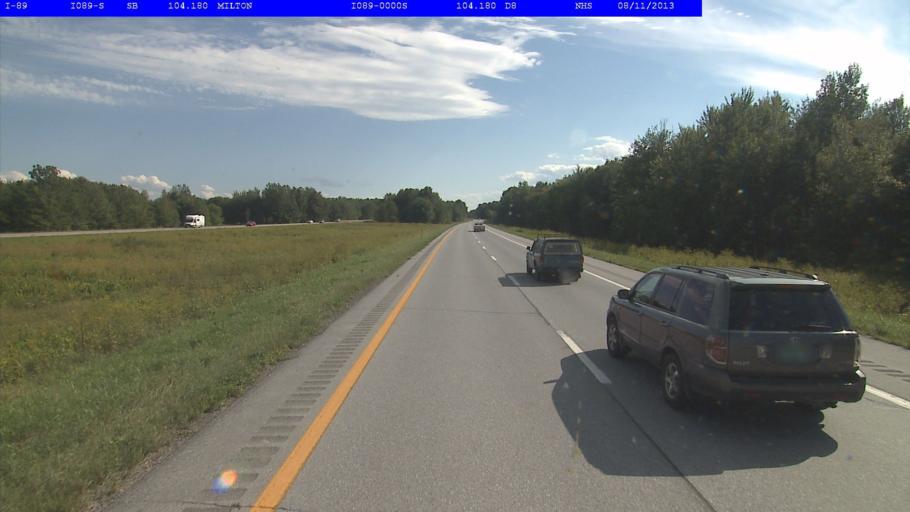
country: US
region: Vermont
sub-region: Chittenden County
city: Milton
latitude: 44.6729
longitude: -73.1326
